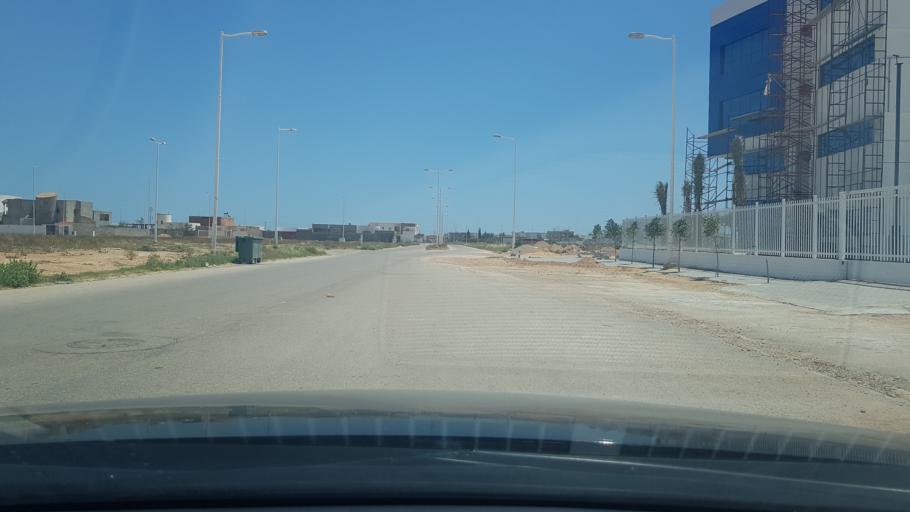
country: TN
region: Safaqis
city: Al Qarmadah
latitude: 34.8325
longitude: 10.7475
